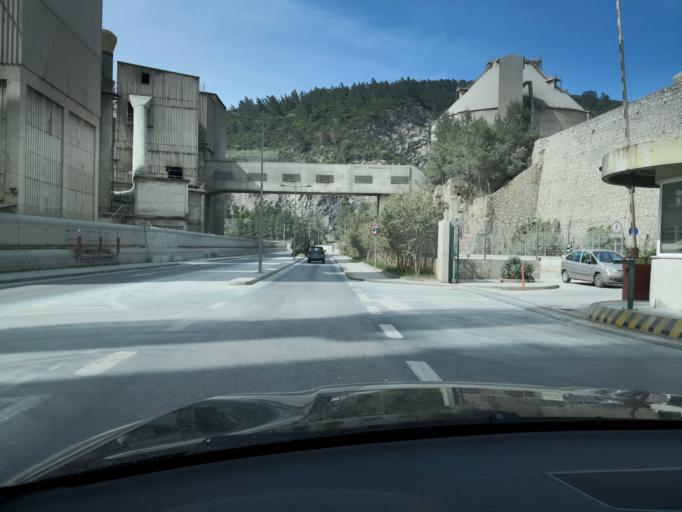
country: PT
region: Setubal
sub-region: Setubal
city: Setubal
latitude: 38.4939
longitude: -8.9326
